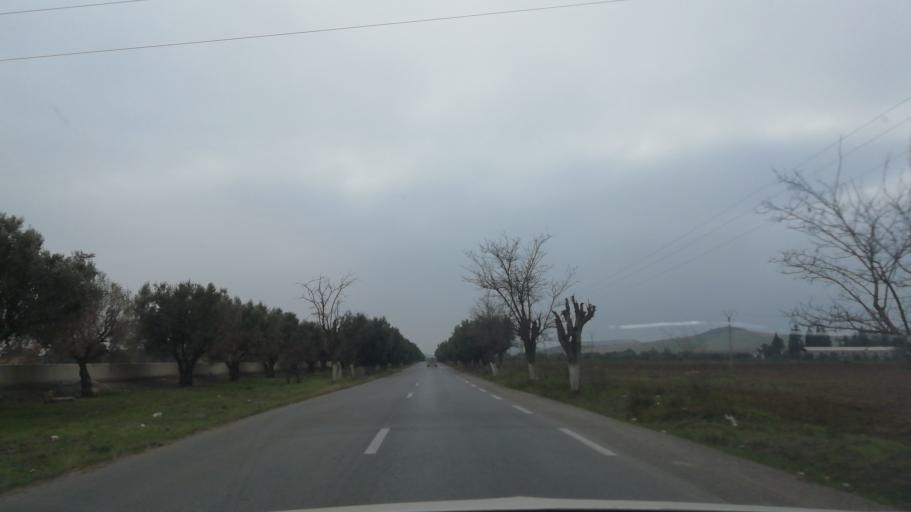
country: DZ
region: Sidi Bel Abbes
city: Sfizef
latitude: 35.2177
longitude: -0.3033
